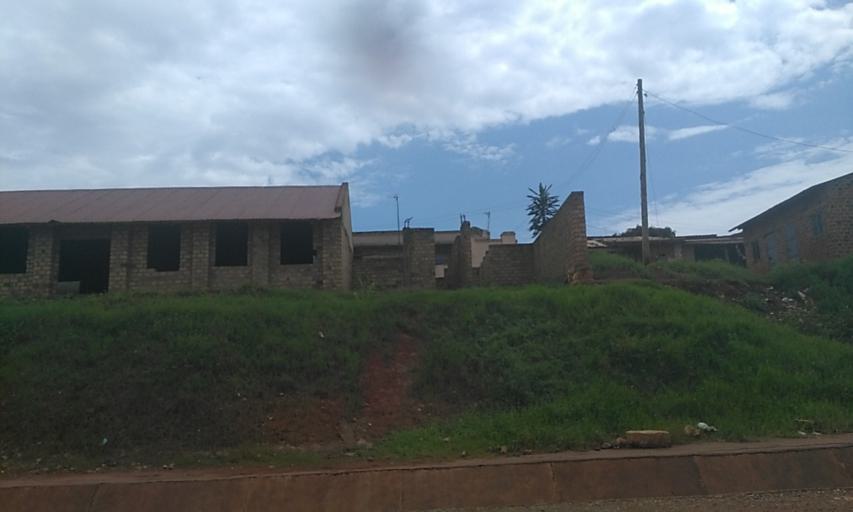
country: UG
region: Central Region
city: Kampala Central Division
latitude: 0.3302
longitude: 32.5262
